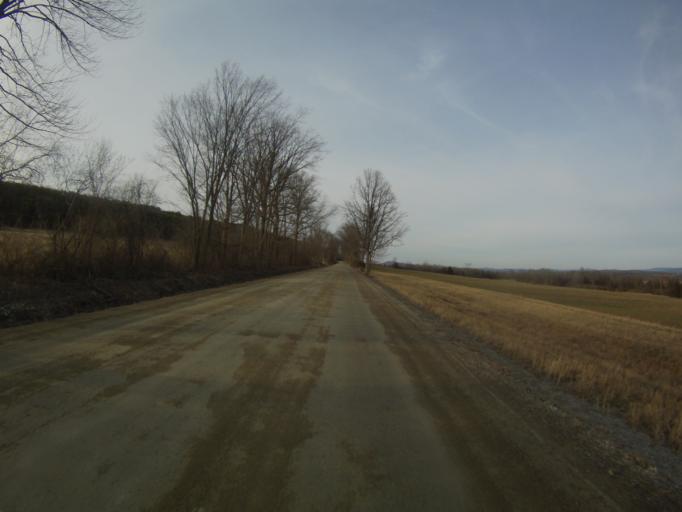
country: US
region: Vermont
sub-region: Addison County
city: Middlebury (village)
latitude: 44.0183
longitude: -73.2565
